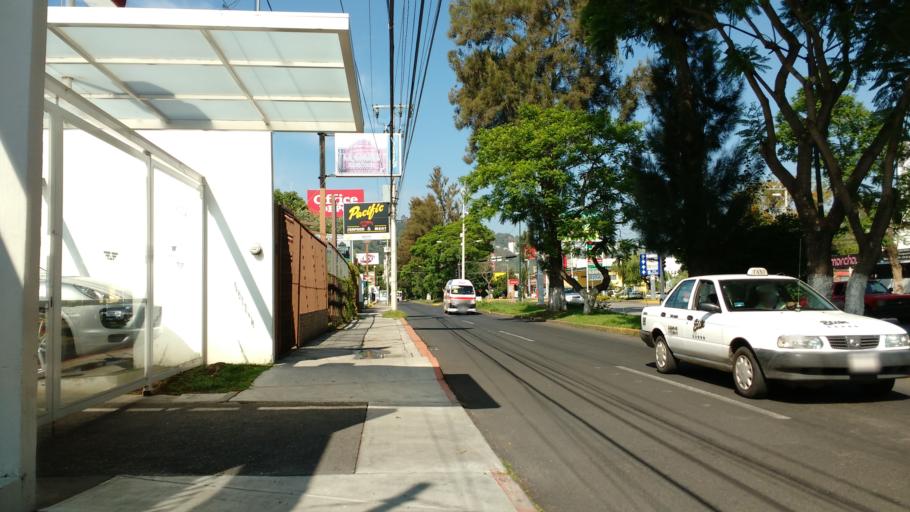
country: MX
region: Michoacan
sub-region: Morelia
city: Montana Monarca (Punta Altozano)
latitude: 19.6846
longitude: -101.1651
